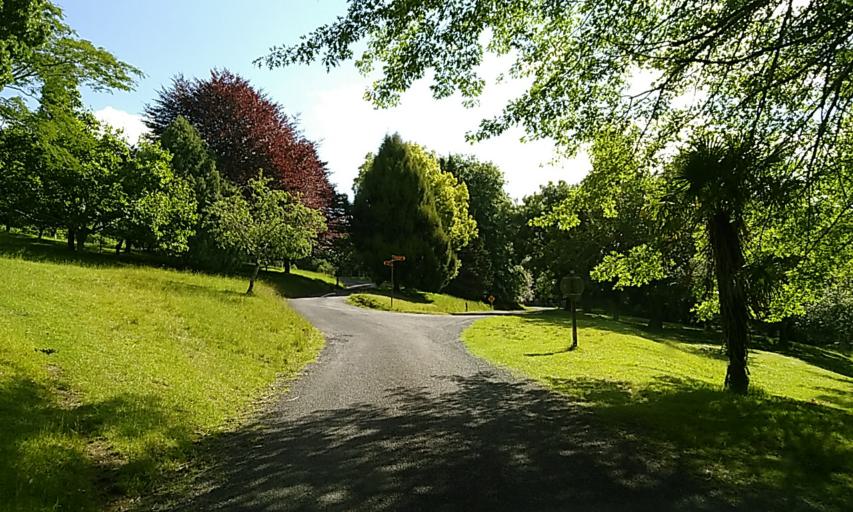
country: NZ
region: Bay of Plenty
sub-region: Tauranga City
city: Tauranga
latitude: -37.8139
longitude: 176.0441
